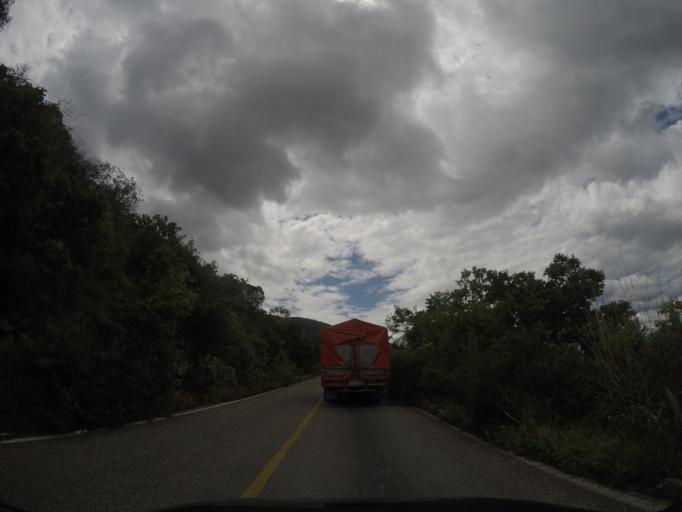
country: MX
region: Oaxaca
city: San Francisco Sola
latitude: 16.4833
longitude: -96.9817
